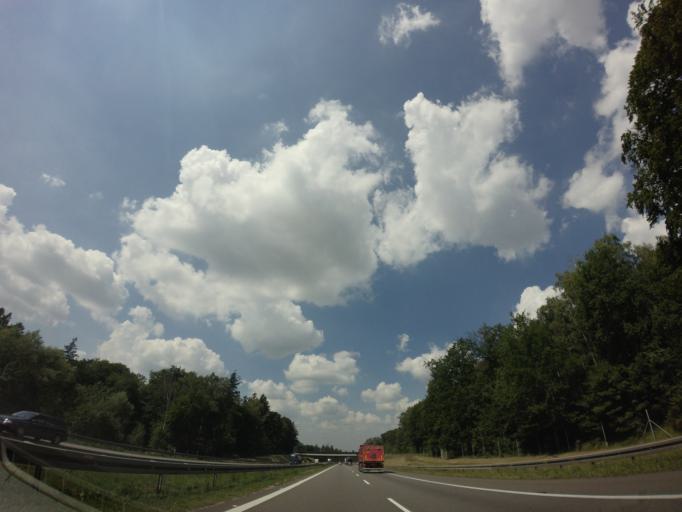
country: PL
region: Opole Voivodeship
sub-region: Powiat krapkowicki
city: Zdzieszowice
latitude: 50.4693
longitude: 18.1464
